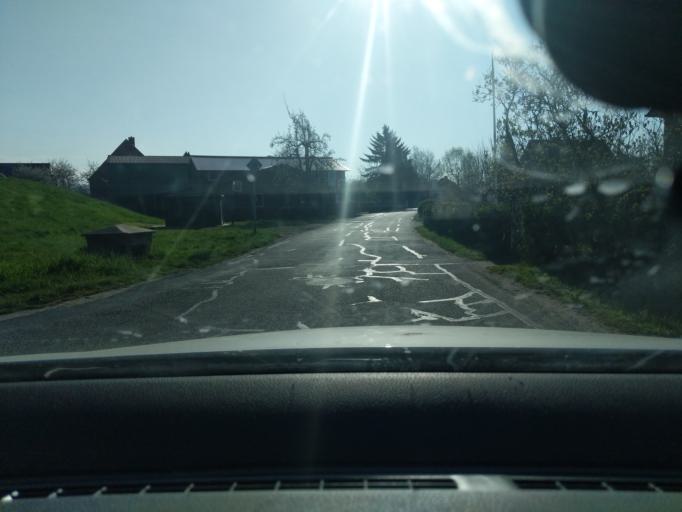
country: DE
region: Lower Saxony
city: Grunendeich
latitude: 53.5665
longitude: 9.6269
